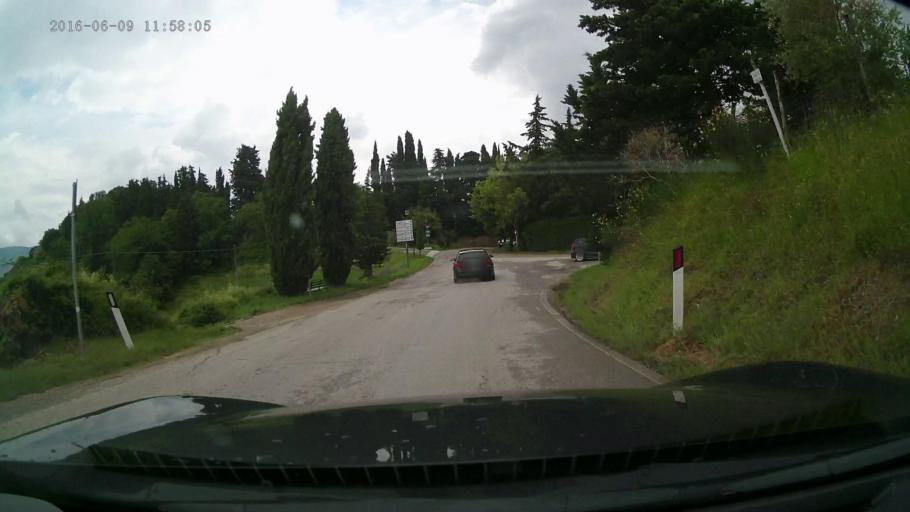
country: IT
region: Tuscany
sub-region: Province of Florence
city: Panzano in Chianti
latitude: 43.5489
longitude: 11.3060
